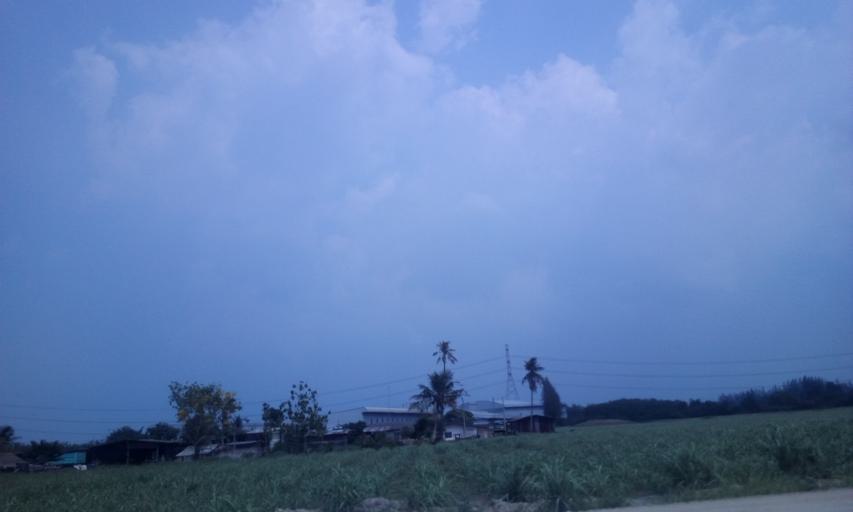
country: TH
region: Chon Buri
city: Ban Bueng
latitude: 13.3343
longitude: 101.1880
